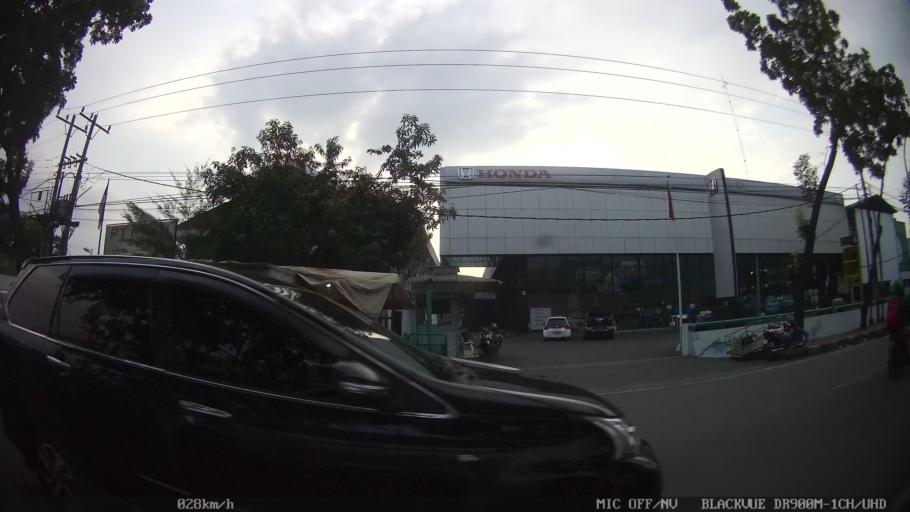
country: ID
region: North Sumatra
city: Medan
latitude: 3.6025
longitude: 98.6686
